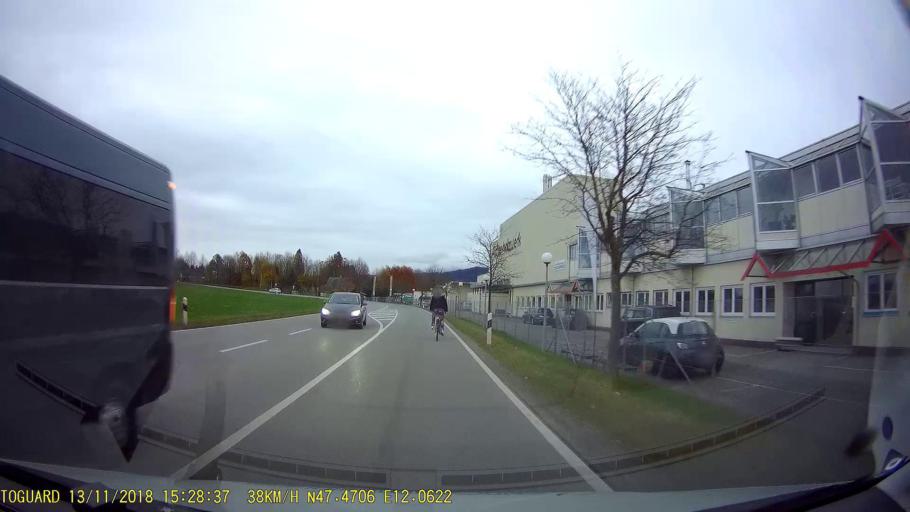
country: DE
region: Bavaria
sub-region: Upper Bavaria
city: Raubling
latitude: 47.7844
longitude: 12.1042
